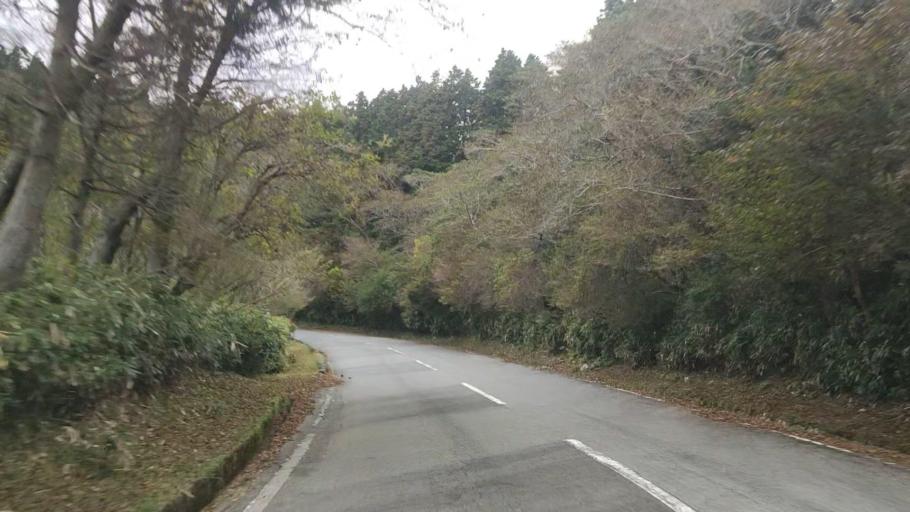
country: JP
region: Shizuoka
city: Heda
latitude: 34.9322
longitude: 138.8403
